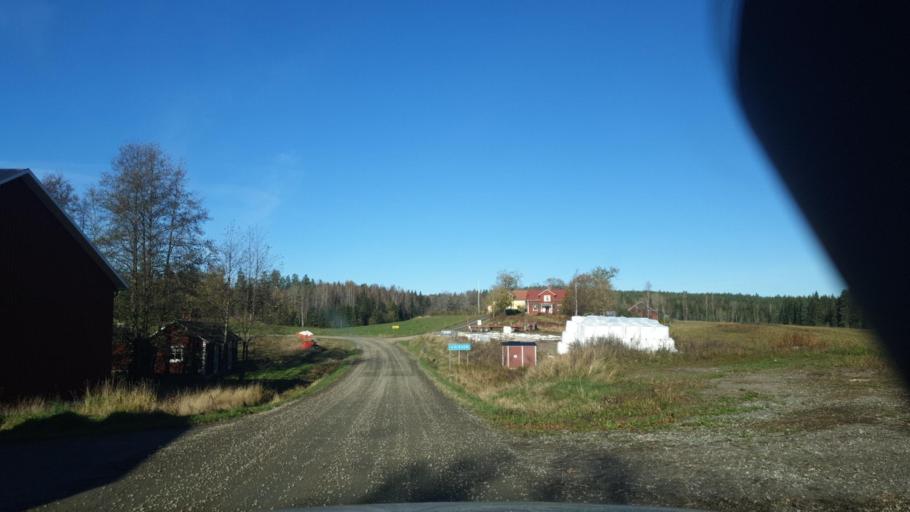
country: SE
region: Vaermland
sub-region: Karlstads Kommun
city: Edsvalla
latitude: 59.5065
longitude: 13.0283
